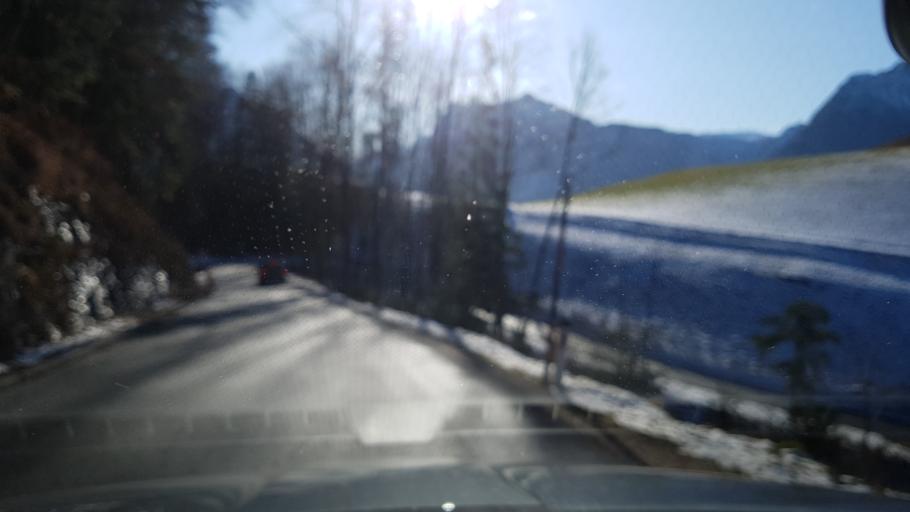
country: AT
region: Salzburg
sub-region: Politischer Bezirk Hallein
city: Golling an der Salzach
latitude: 47.6225
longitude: 13.1853
